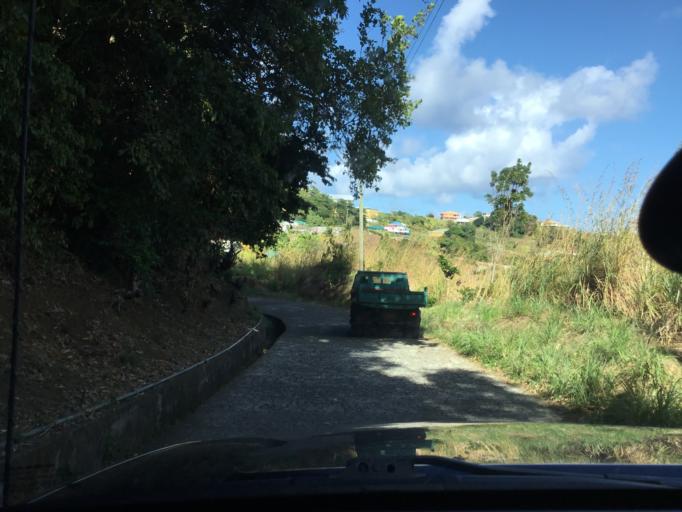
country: VC
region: Charlotte
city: Biabou
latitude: 13.1588
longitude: -61.1687
